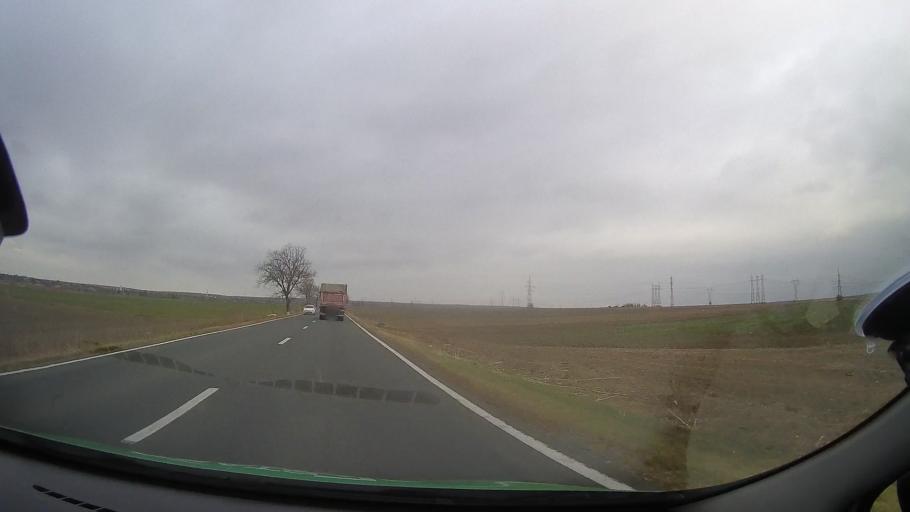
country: RO
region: Constanta
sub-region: Comuna Castelu
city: Castelu
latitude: 44.2540
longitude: 28.3529
